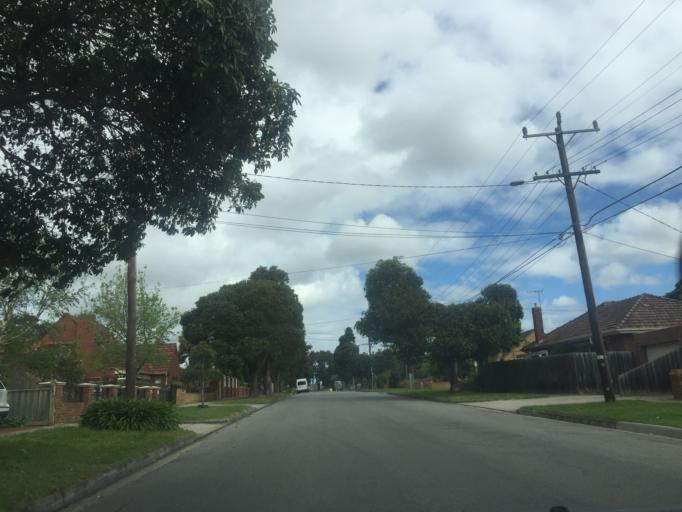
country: AU
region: Victoria
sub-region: Darebin
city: Reservoir
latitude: -37.7213
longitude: 145.0162
